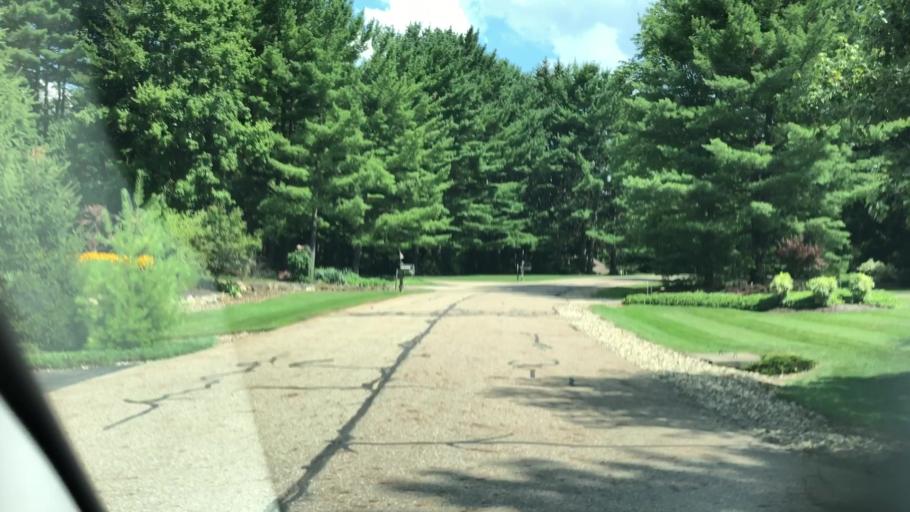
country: US
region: Ohio
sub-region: Summit County
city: Montrose-Ghent
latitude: 41.1638
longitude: -81.6432
